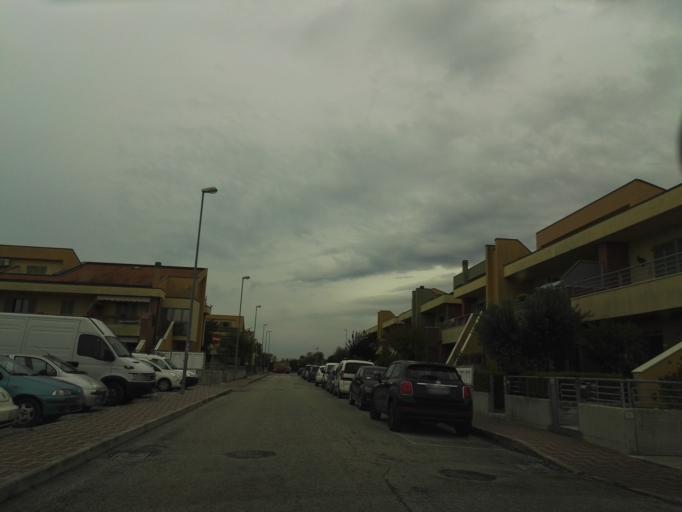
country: IT
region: The Marches
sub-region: Provincia di Pesaro e Urbino
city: Marotta
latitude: 43.7626
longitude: 13.1409
